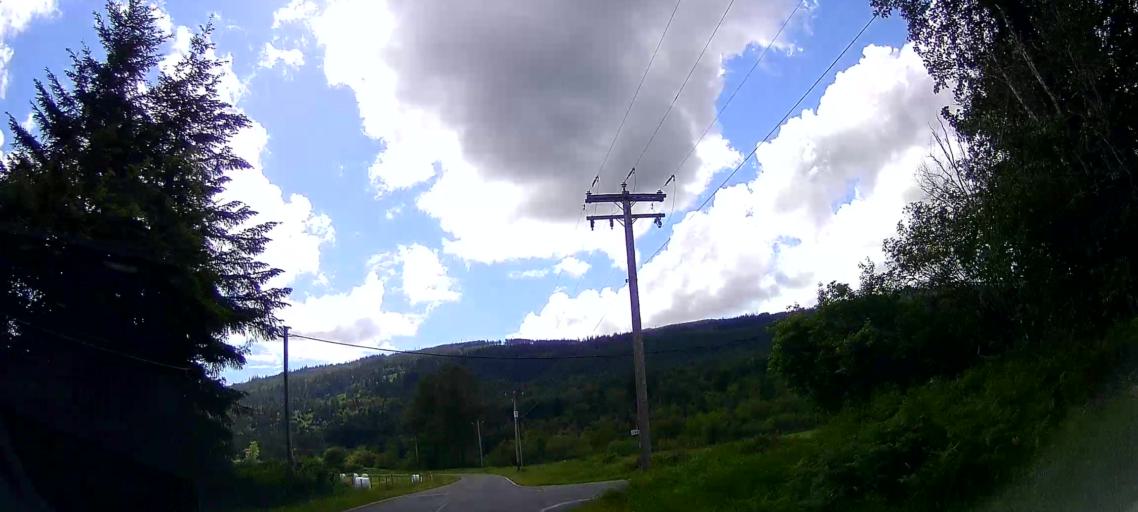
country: US
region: Washington
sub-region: Whatcom County
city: Sudden Valley
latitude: 48.6888
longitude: -122.1870
